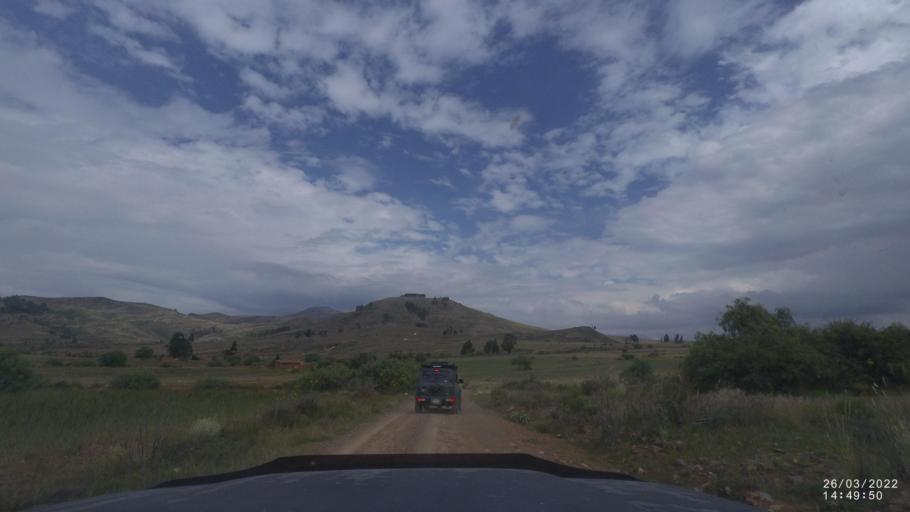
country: BO
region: Cochabamba
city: Cliza
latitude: -17.7268
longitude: -65.8505
